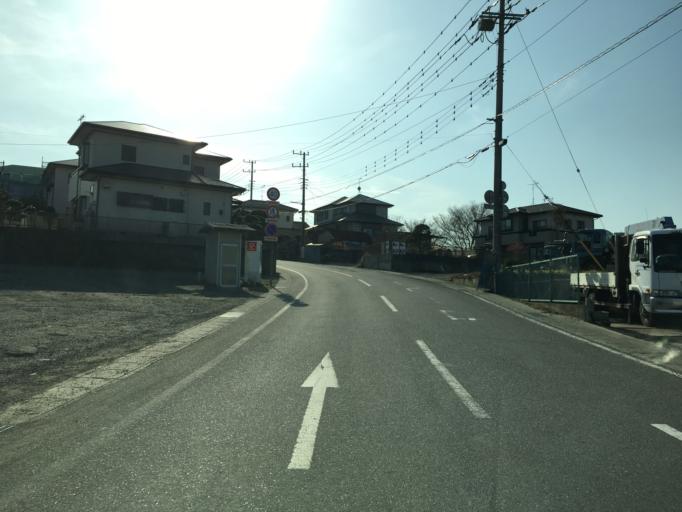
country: JP
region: Ibaraki
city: Kitaibaraki
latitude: 36.7718
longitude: 140.7260
